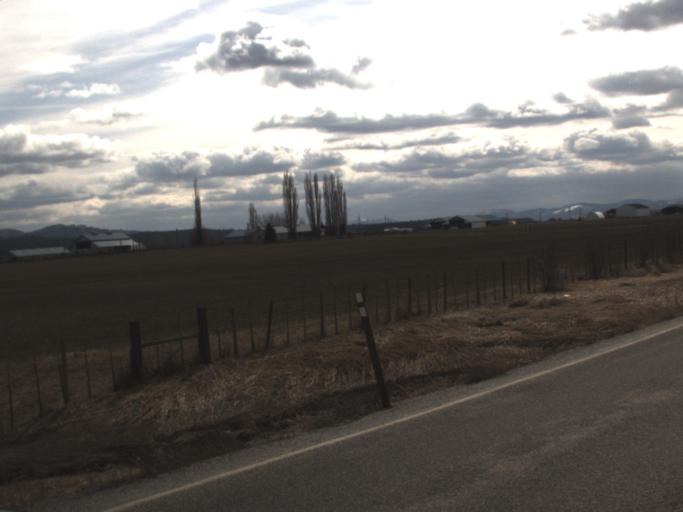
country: US
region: Washington
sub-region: Pend Oreille County
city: Newport
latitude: 48.3634
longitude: -117.3047
